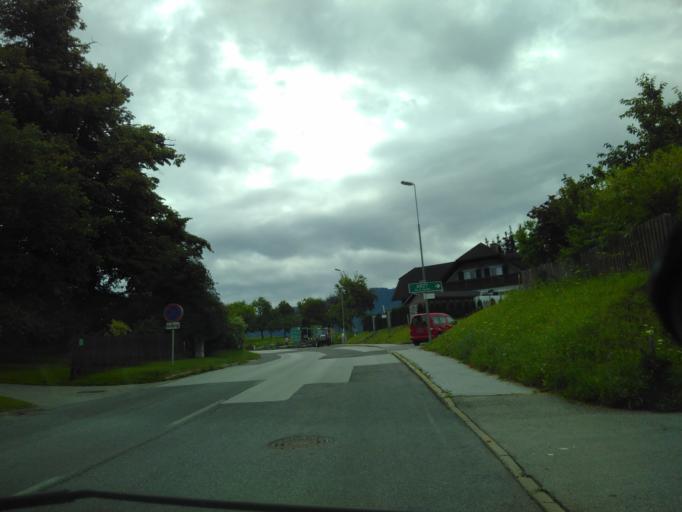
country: AT
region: Styria
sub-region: Politischer Bezirk Graz-Umgebung
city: Semriach
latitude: 47.2167
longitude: 15.4102
